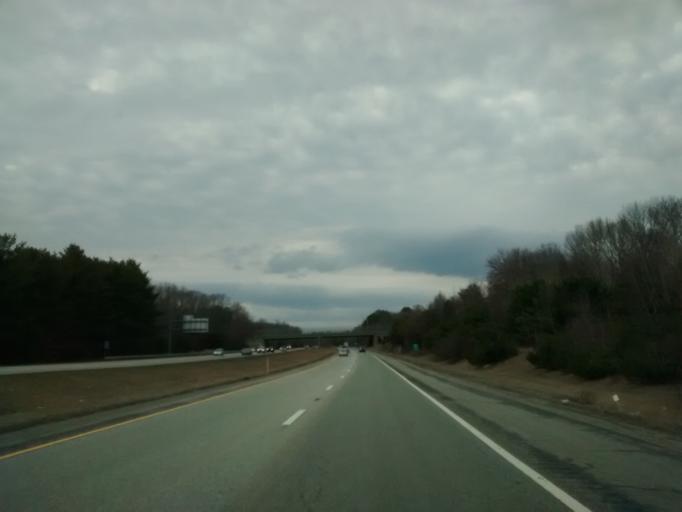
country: US
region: Massachusetts
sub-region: Worcester County
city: Uxbridge
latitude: 42.0483
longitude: -71.6297
